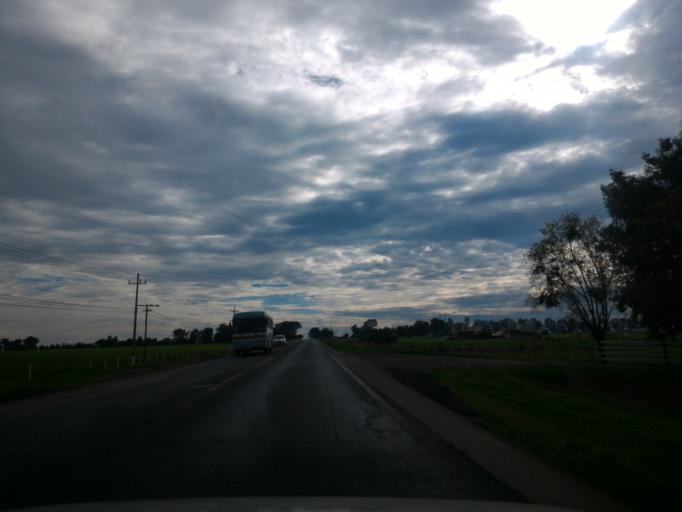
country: MX
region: Jalisco
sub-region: Acatic
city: Tierras Coloradas
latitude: 20.7279
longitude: -102.8786
